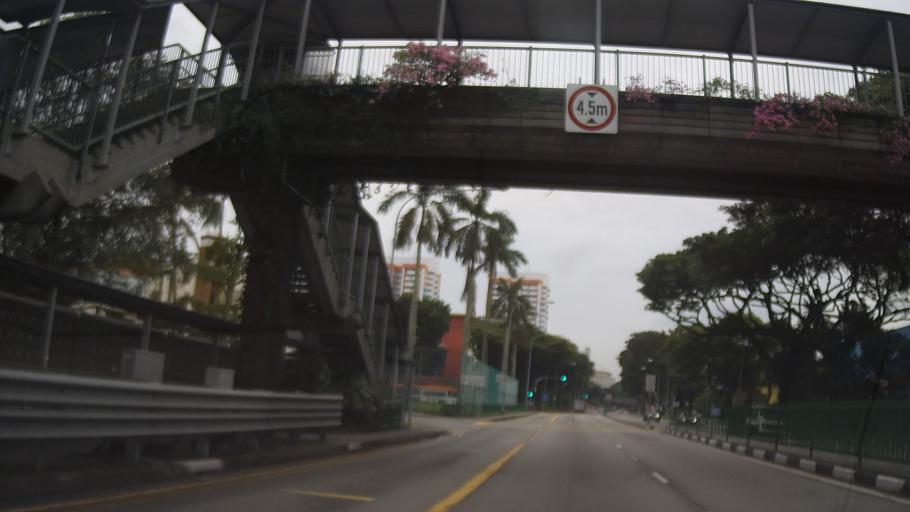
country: SG
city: Singapore
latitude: 1.3266
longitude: 103.8805
